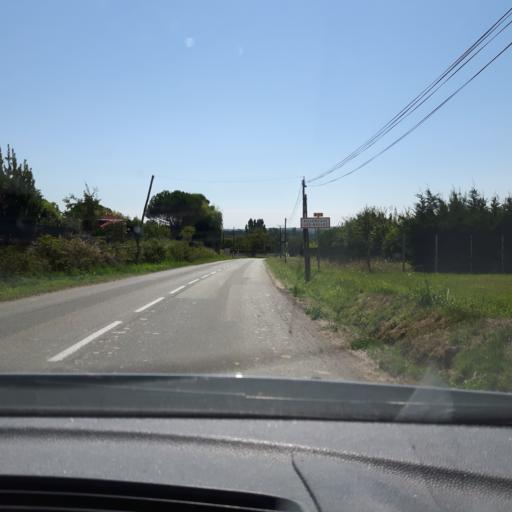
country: FR
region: Midi-Pyrenees
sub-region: Departement de la Haute-Garonne
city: Bouloc
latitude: 43.7693
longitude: 1.3961
